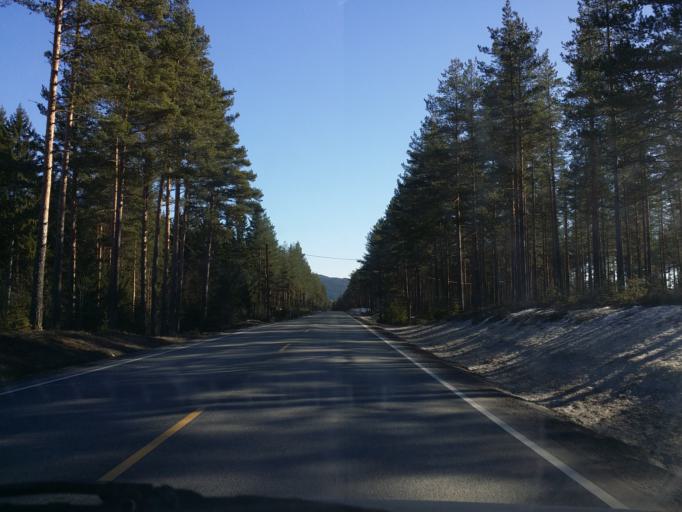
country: NO
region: Buskerud
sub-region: Ringerike
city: Honefoss
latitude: 60.3097
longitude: 10.1579
